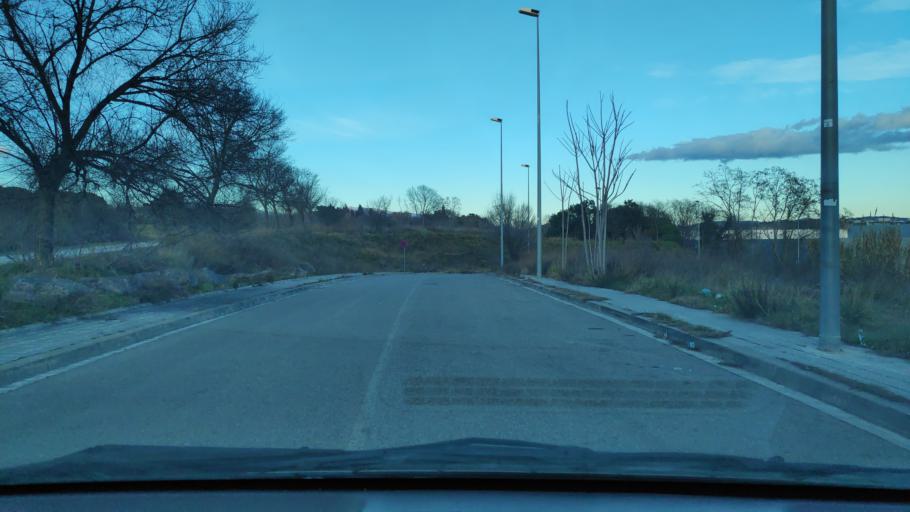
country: ES
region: Catalonia
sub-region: Provincia de Barcelona
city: Llica de Vall
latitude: 41.5718
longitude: 2.2656
